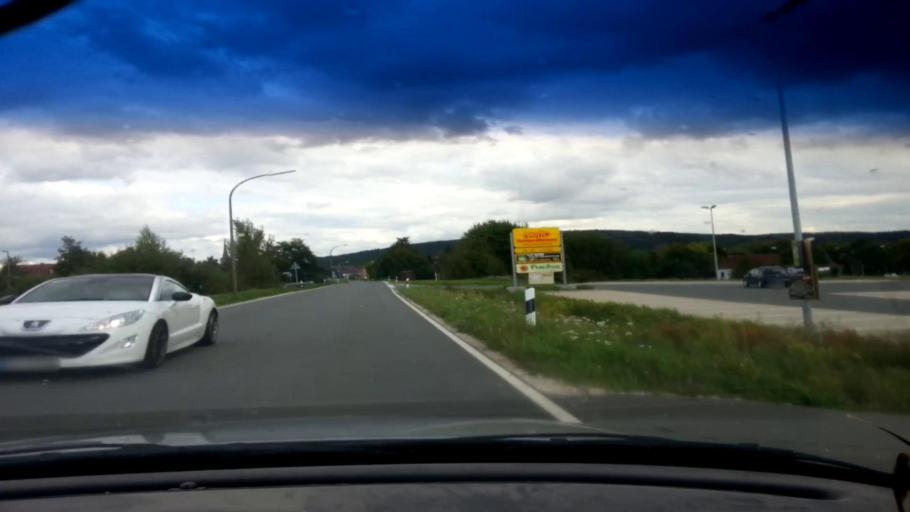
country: DE
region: Bavaria
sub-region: Upper Franconia
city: Rattelsdorf
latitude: 50.0121
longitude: 10.8976
